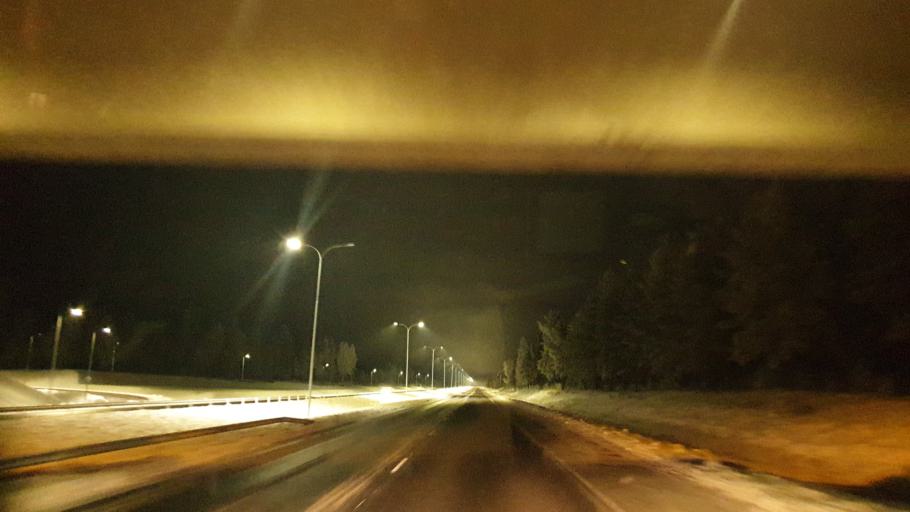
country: FI
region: Northern Ostrobothnia
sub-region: Oulu
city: Haukipudas
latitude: 65.1618
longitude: 25.4273
